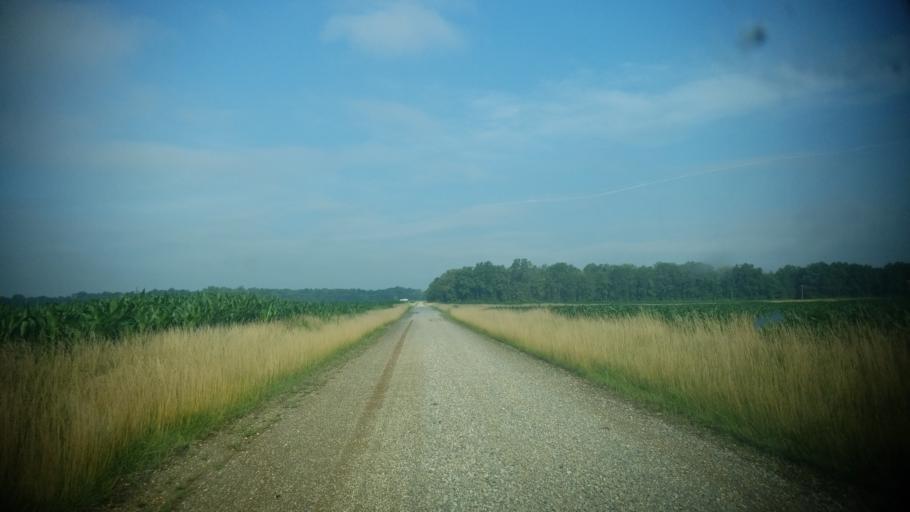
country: US
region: Illinois
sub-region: Clay County
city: Flora
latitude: 38.6018
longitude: -88.3538
